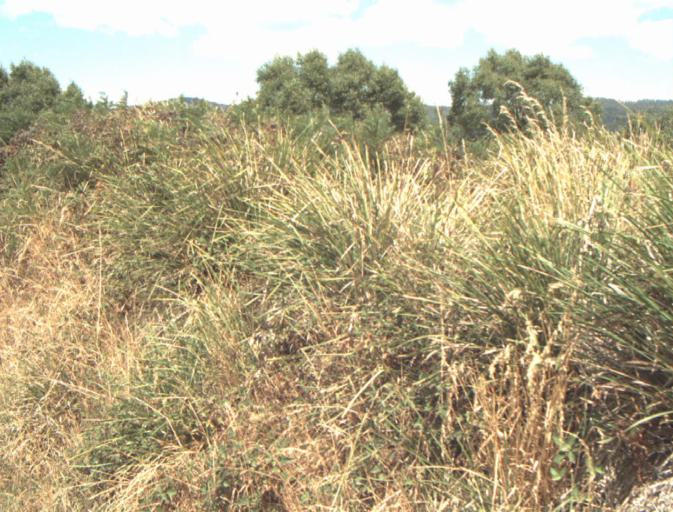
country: AU
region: Tasmania
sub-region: Launceston
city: Mayfield
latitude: -41.2102
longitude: 147.1497
